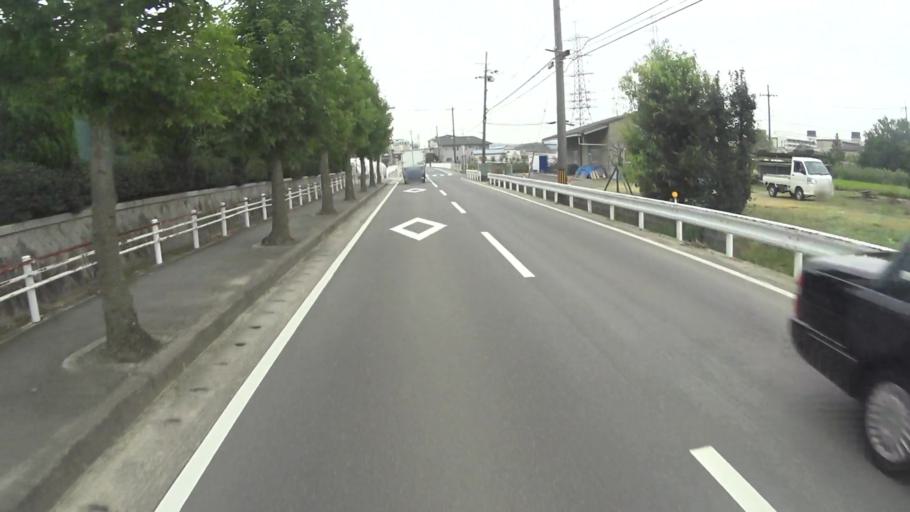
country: JP
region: Kyoto
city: Tanabe
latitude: 34.8438
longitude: 135.7648
